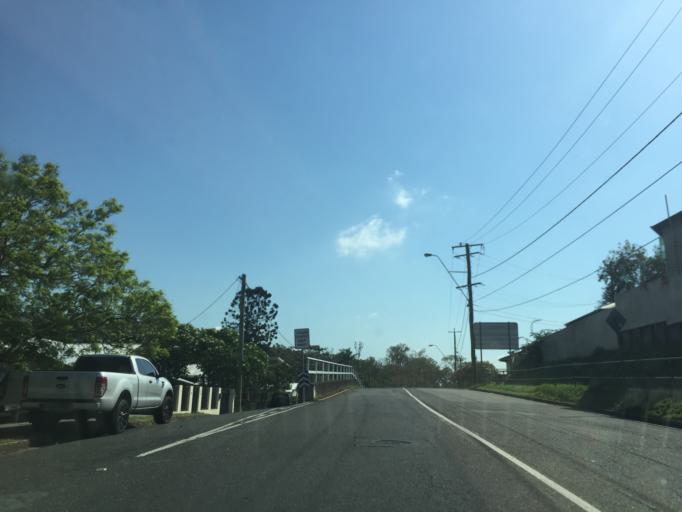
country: AU
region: Queensland
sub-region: Brisbane
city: Milton
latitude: -27.4672
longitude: 152.9885
